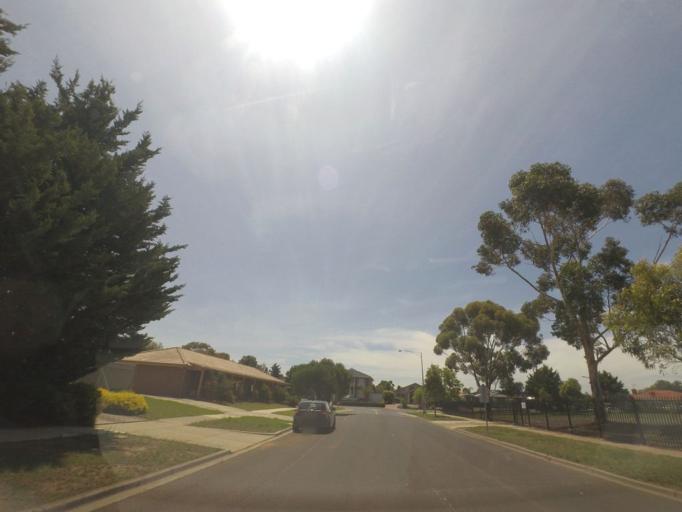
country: AU
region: Victoria
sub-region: Brimbank
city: Taylors Lakes
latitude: -37.7074
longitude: 144.7906
